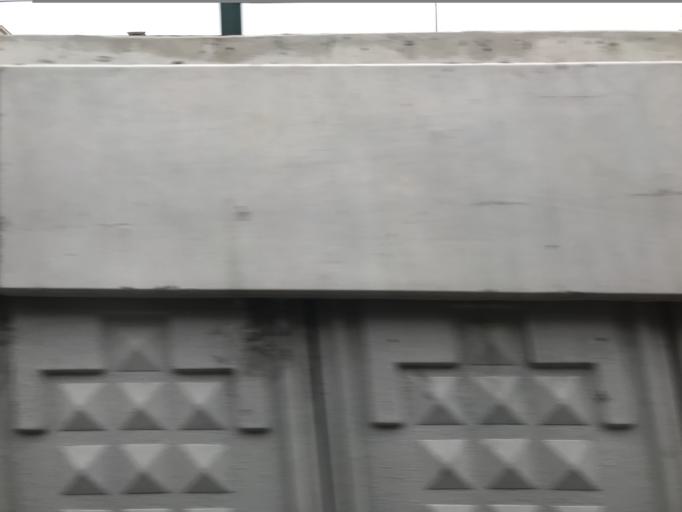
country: TR
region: Istanbul
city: Bahcelievler
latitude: 40.9661
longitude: 28.7987
